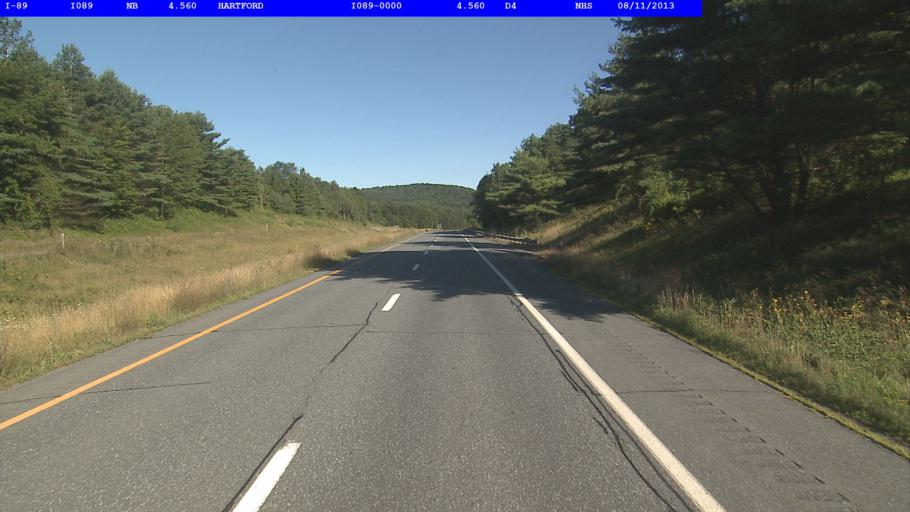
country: US
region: Vermont
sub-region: Windsor County
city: White River Junction
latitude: 43.6735
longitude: -72.3936
